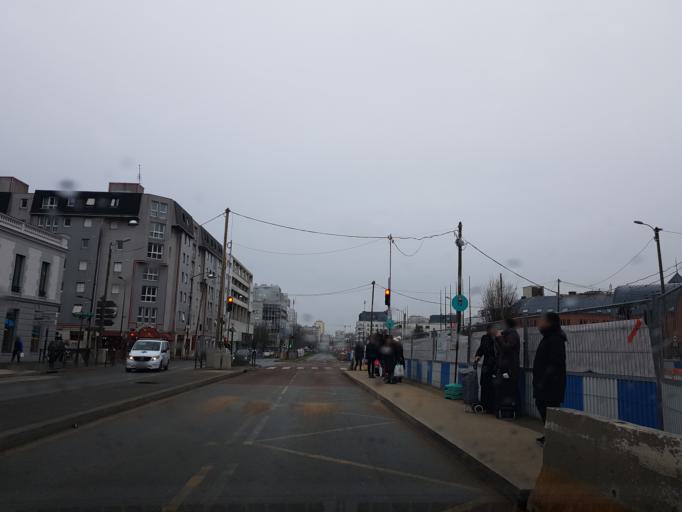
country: FR
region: Ile-de-France
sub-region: Departement du Val-de-Marne
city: Vitry-sur-Seine
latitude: 48.7898
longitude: 2.3888
